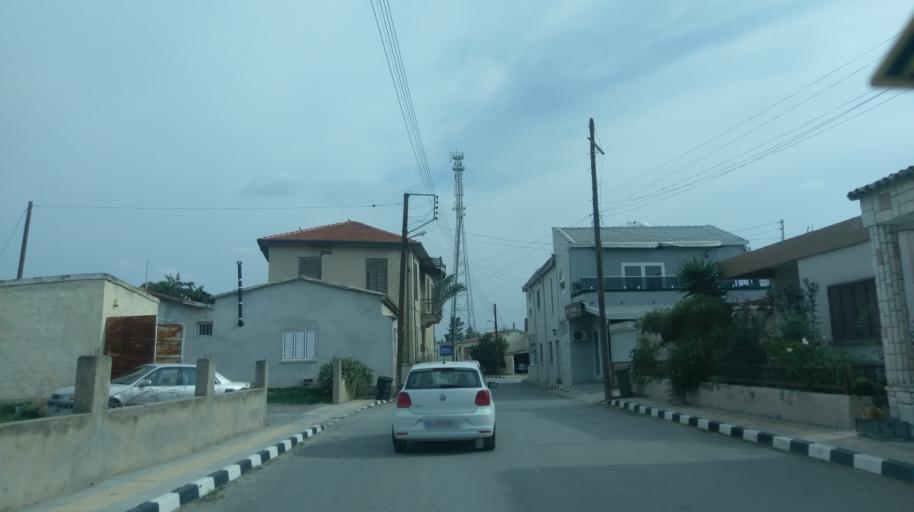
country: CY
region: Ammochostos
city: Lefkonoiko
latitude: 35.2600
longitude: 33.7280
